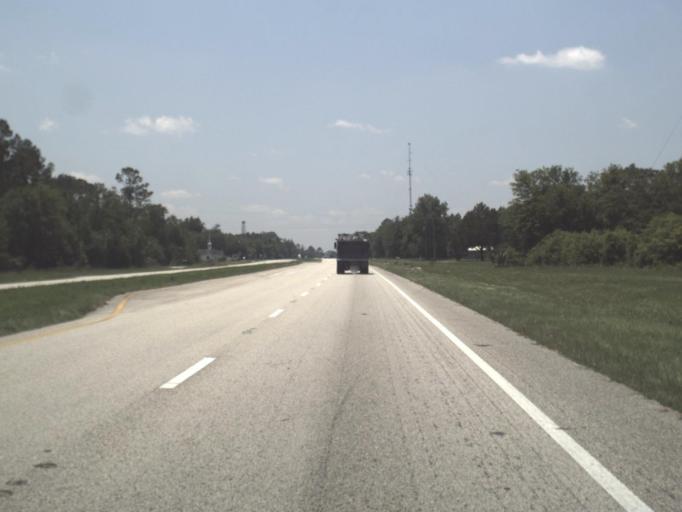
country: US
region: Florida
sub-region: Bradford County
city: Starke
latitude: 30.1154
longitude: -82.0477
